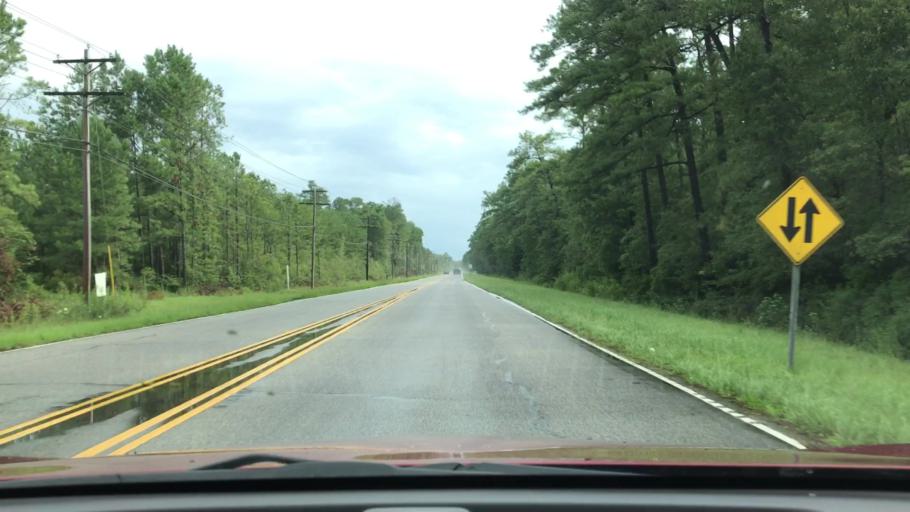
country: US
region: South Carolina
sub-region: Georgetown County
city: Georgetown
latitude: 33.4204
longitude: -79.2826
